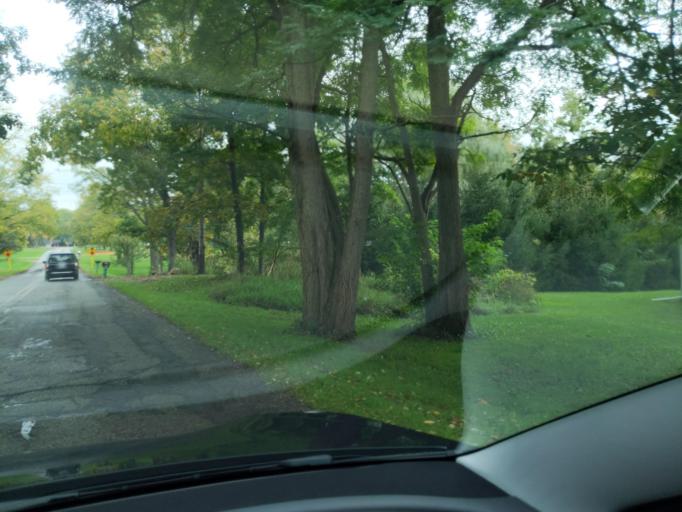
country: US
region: Michigan
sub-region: Ingham County
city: Leslie
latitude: 42.4121
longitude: -84.3784
